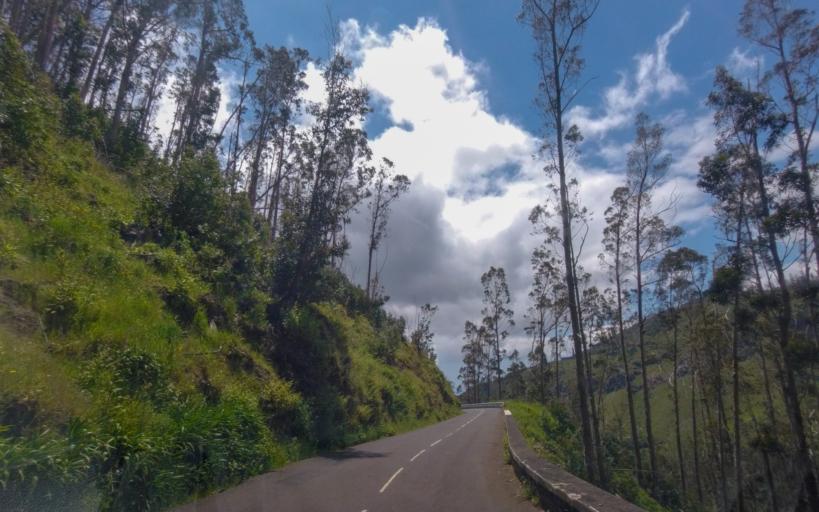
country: PT
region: Madeira
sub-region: Funchal
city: Nossa Senhora do Monte
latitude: 32.6872
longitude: -16.8897
